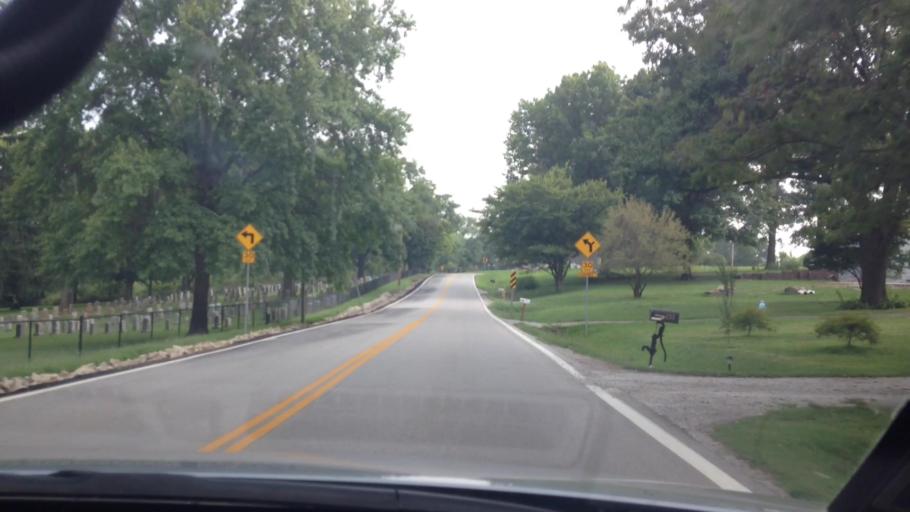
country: US
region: Kansas
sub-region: Leavenworth County
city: Lansing
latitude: 39.2688
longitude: -94.8905
